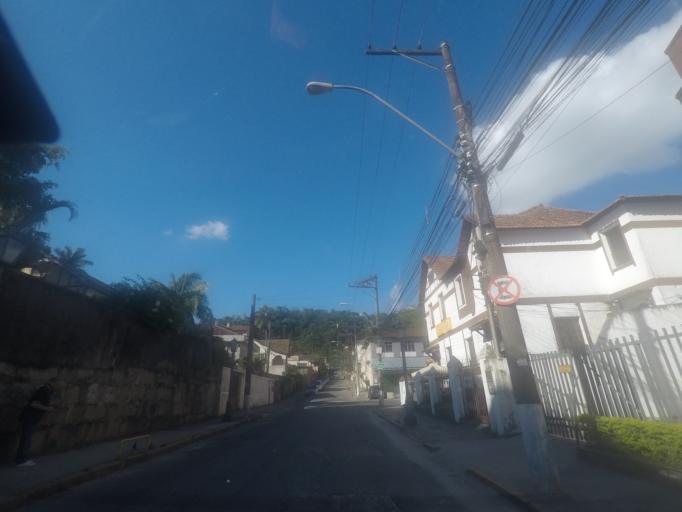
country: BR
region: Rio de Janeiro
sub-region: Petropolis
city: Petropolis
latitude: -22.5070
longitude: -43.1664
